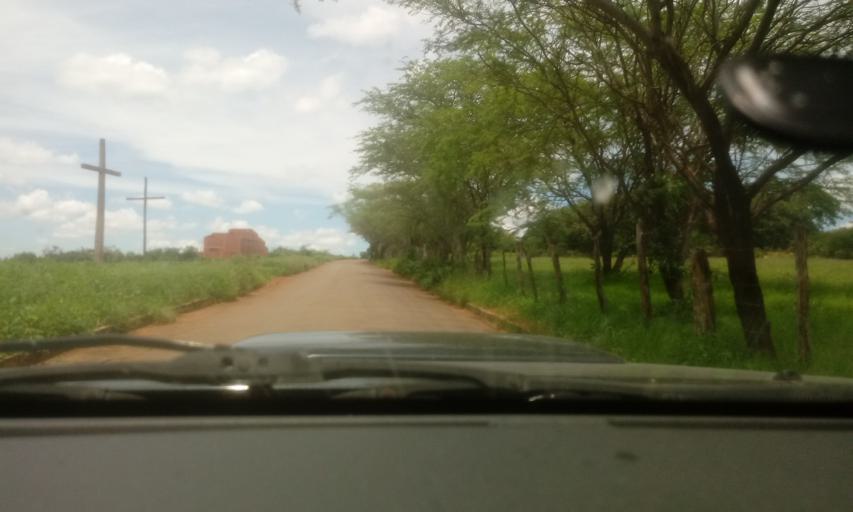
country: BR
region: Bahia
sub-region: Riacho De Santana
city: Riacho de Santana
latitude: -13.5991
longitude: -42.9441
